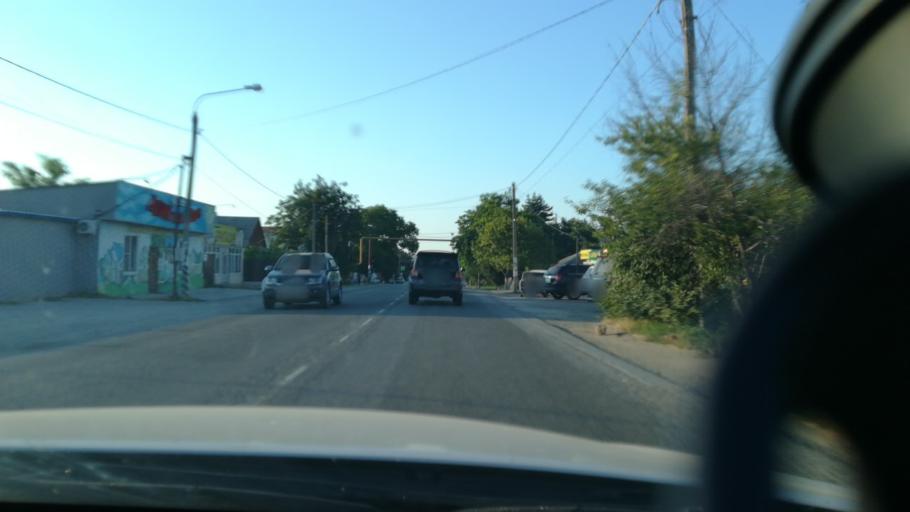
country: RU
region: Krasnodarskiy
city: Gostagayevskaya
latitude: 45.0222
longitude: 37.5029
